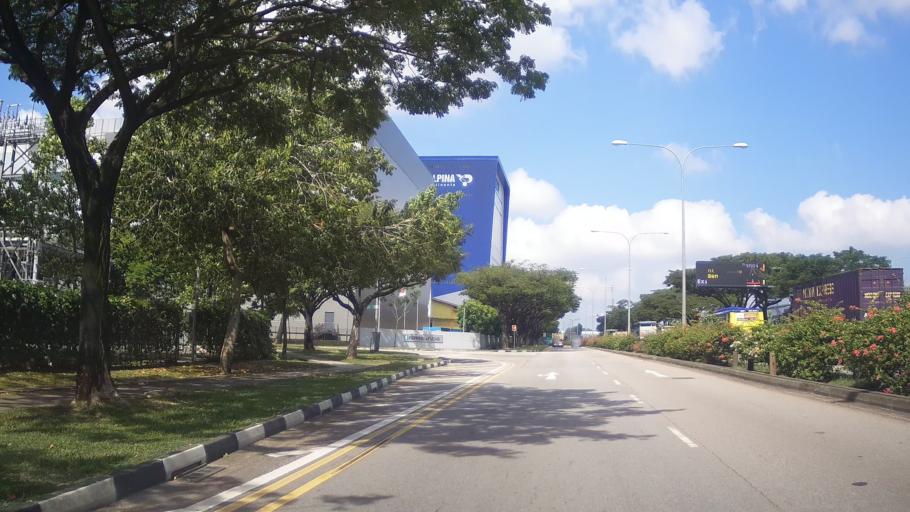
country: SG
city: Singapore
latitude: 1.3219
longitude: 103.7026
